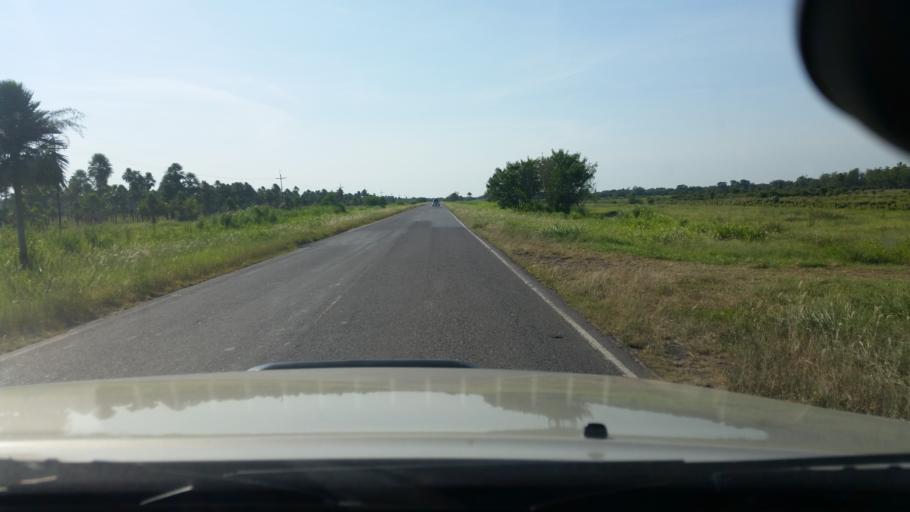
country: PY
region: Presidente Hayes
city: Benjamin Aceval
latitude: -24.7891
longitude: -57.8001
